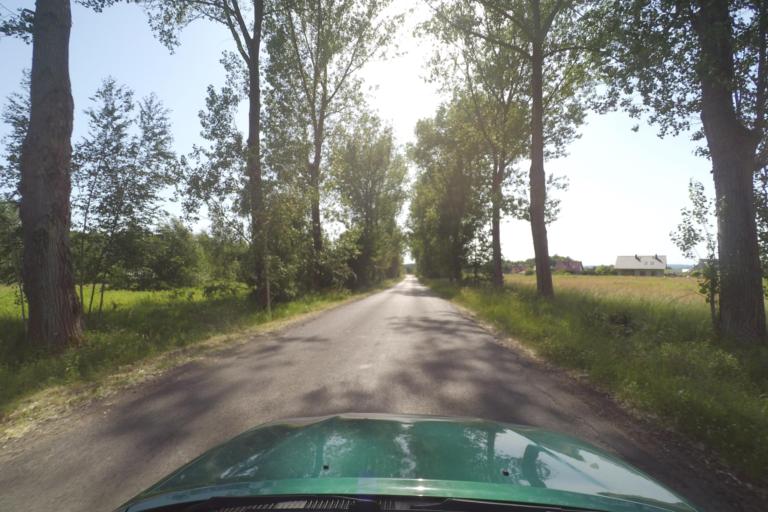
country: PL
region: Lower Silesian Voivodeship
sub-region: Powiat lubanski
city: Luban
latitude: 51.1240
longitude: 15.3330
